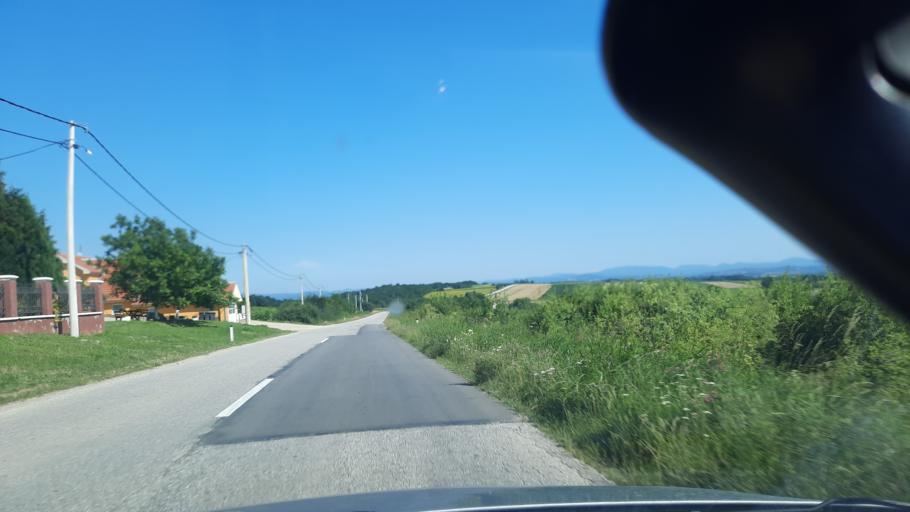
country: RS
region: Central Serbia
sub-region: Branicevski Okrug
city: Malo Crnice
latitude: 44.5840
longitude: 21.4116
